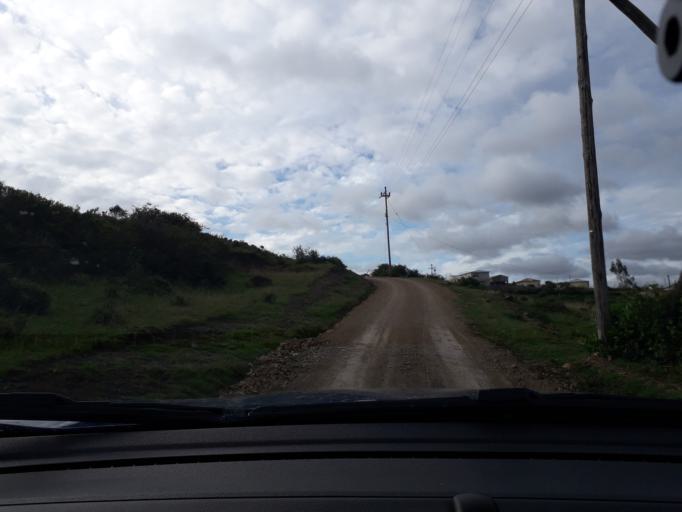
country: ZA
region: Eastern Cape
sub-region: Buffalo City Metropolitan Municipality
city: East London
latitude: -32.8015
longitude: 27.9621
